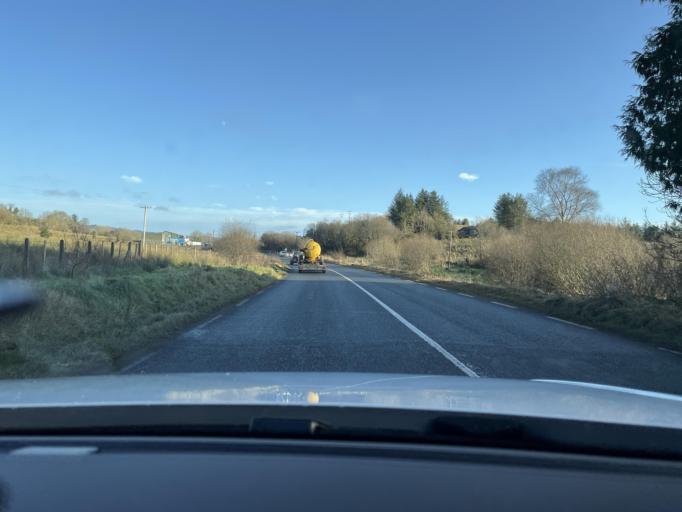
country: IE
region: Connaught
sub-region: County Leitrim
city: Manorhamilton
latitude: 54.1984
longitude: -8.1857
